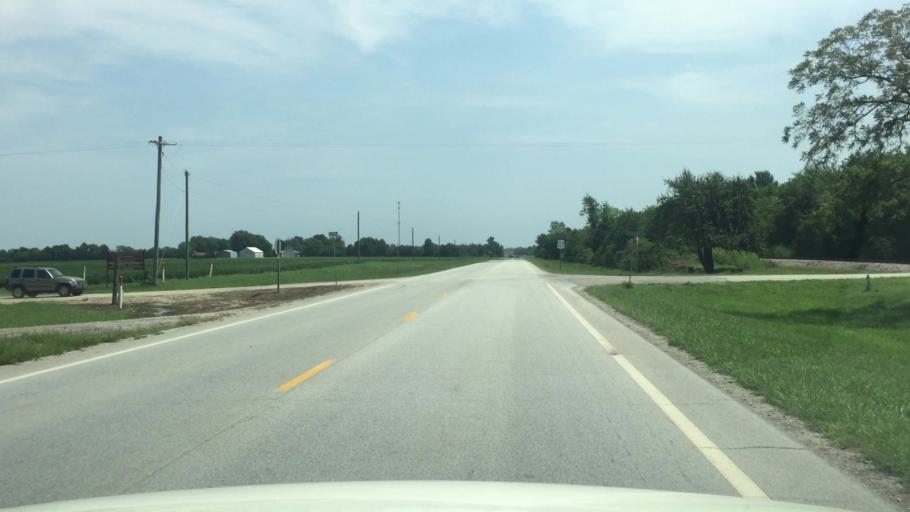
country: US
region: Kansas
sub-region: Cherokee County
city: Columbus
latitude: 37.1787
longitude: -94.8685
